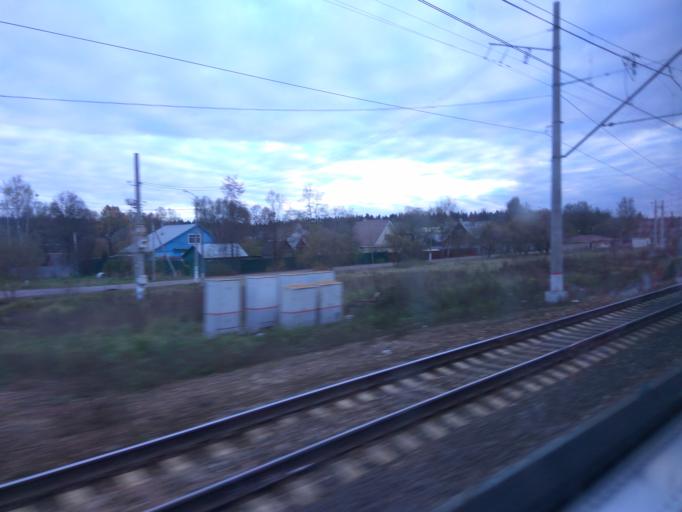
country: RU
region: Moskovskaya
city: Selyatino
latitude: 55.4816
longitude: 36.9186
